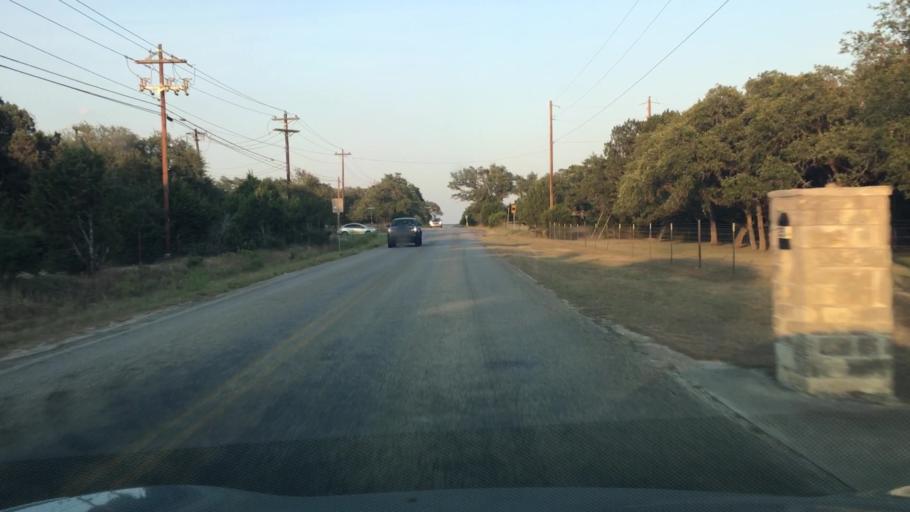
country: US
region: Texas
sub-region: Hays County
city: Dripping Springs
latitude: 30.1535
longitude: -98.0100
